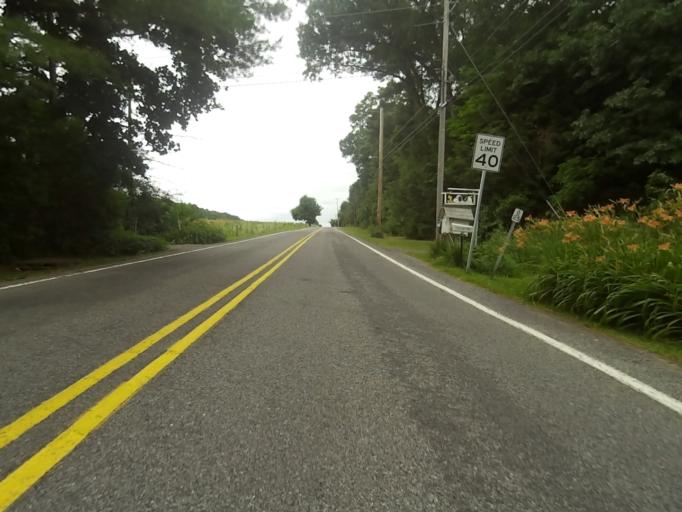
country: US
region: Pennsylvania
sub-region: Centre County
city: Stormstown
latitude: 40.7154
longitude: -78.0039
